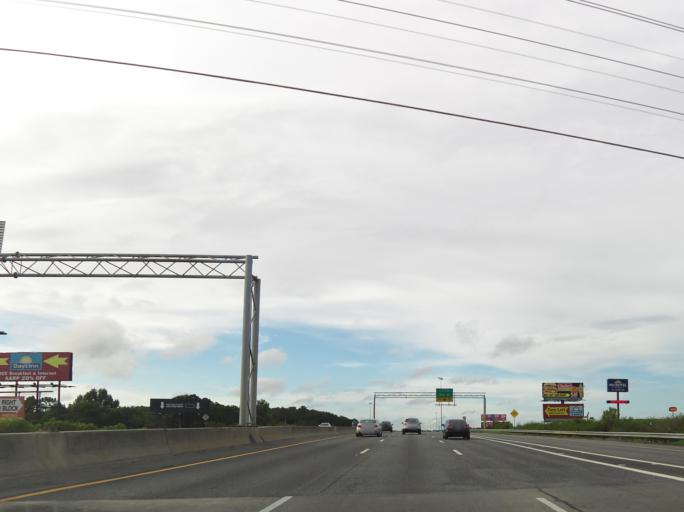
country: US
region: Georgia
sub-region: Tift County
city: Tifton
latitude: 31.4504
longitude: -83.5307
